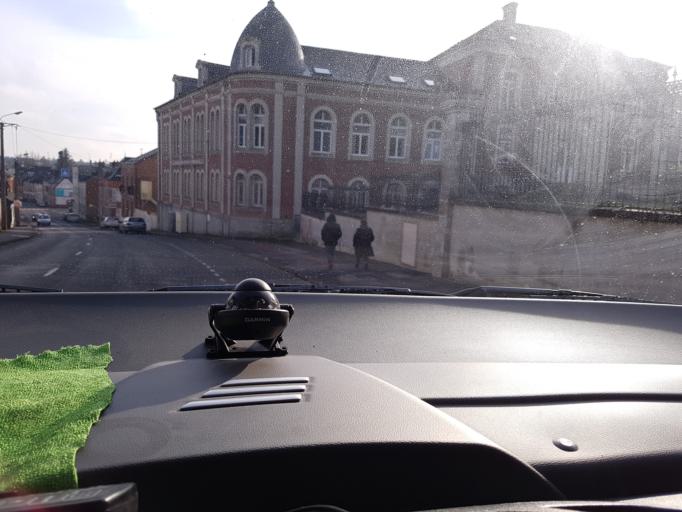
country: FR
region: Picardie
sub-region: Departement de l'Aisne
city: Hirson
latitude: 49.9264
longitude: 4.0759
